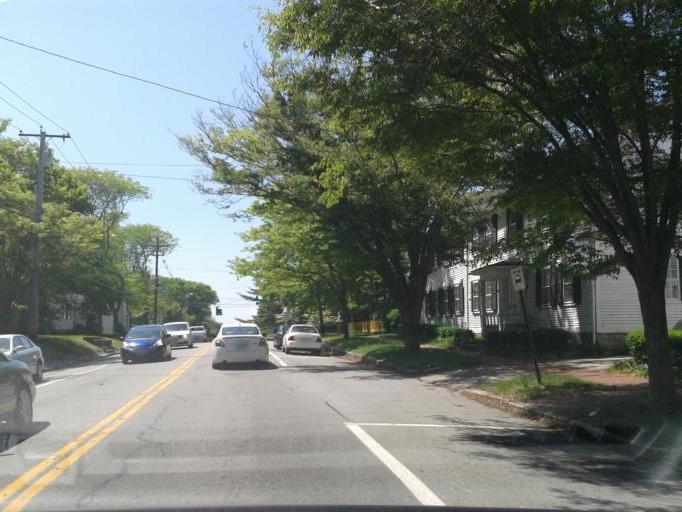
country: US
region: Rhode Island
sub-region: Washington County
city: Kingston
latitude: 41.4802
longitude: -71.5240
